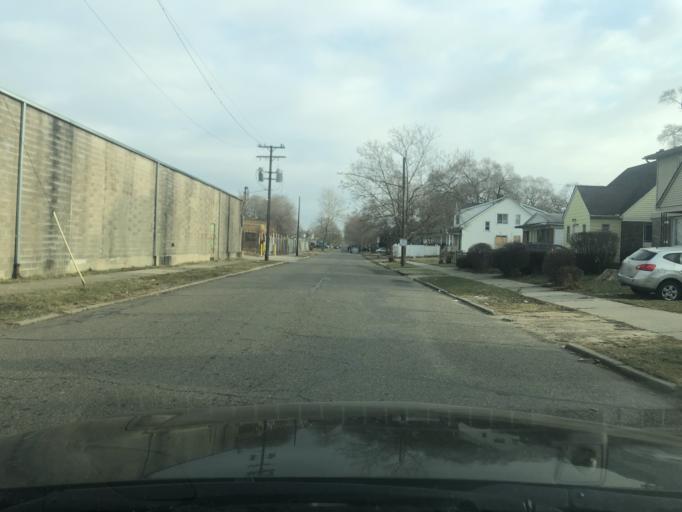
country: US
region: Michigan
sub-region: Wayne County
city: Highland Park
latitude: 42.3955
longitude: -83.1339
